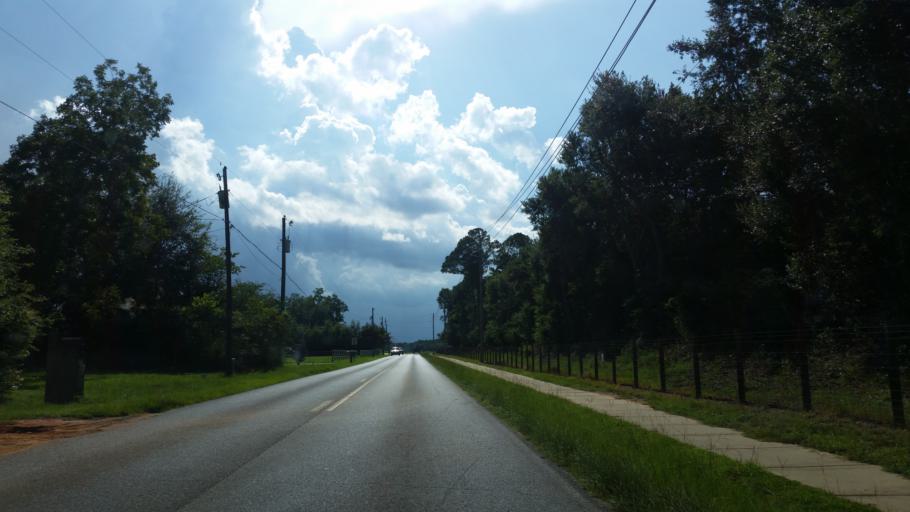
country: US
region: Florida
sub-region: Santa Rosa County
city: Pace
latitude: 30.6184
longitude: -87.1458
